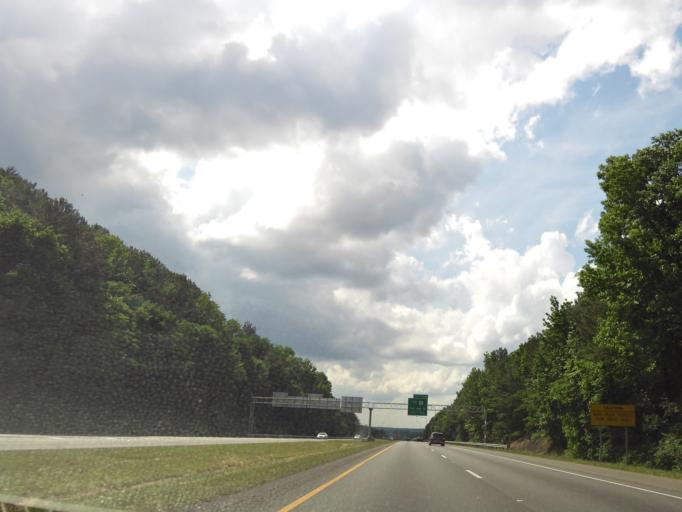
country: US
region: Alabama
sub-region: Jefferson County
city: Irondale
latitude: 33.5359
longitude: -86.7236
